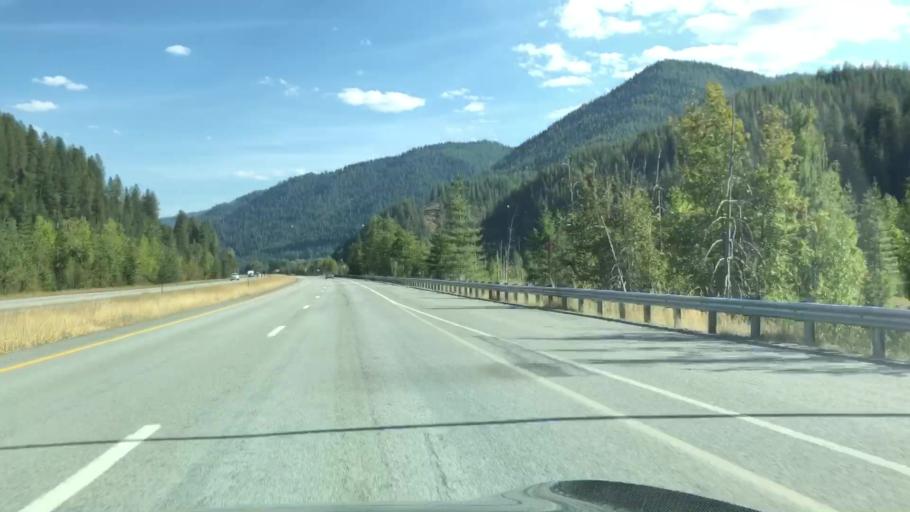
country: US
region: Idaho
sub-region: Shoshone County
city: Osburn
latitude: 47.5248
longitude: -116.0456
